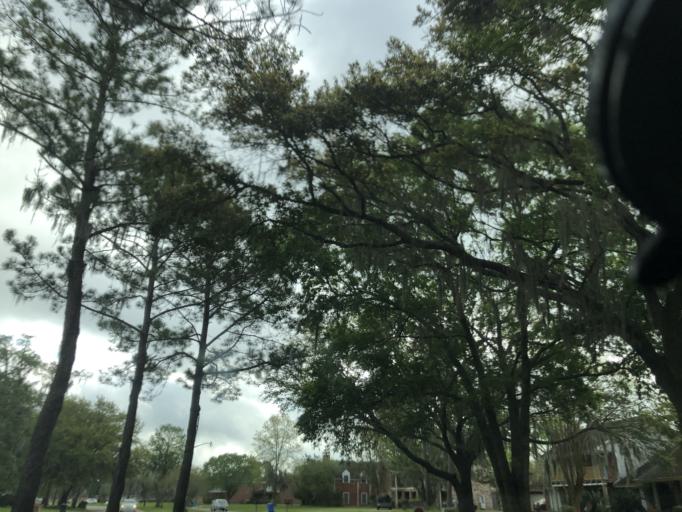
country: US
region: Louisiana
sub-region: Saint Charles Parish
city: New Sarpy
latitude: 29.9696
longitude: -90.3694
